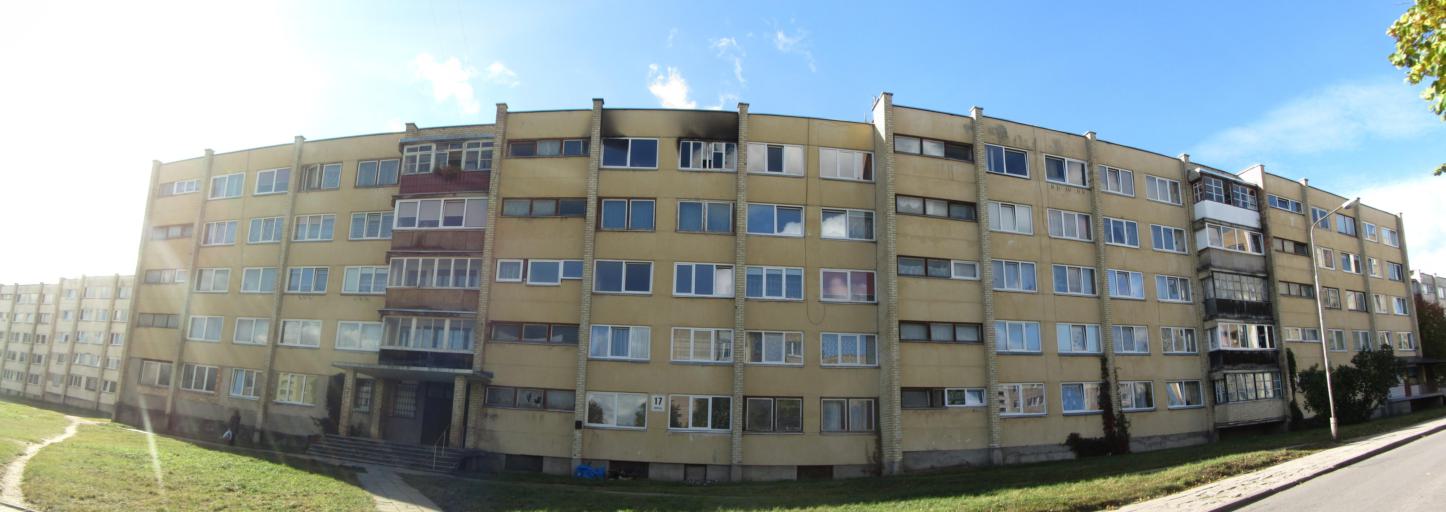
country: LT
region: Utenos apskritis
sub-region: Utena
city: Utena
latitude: 55.4994
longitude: 25.6169
